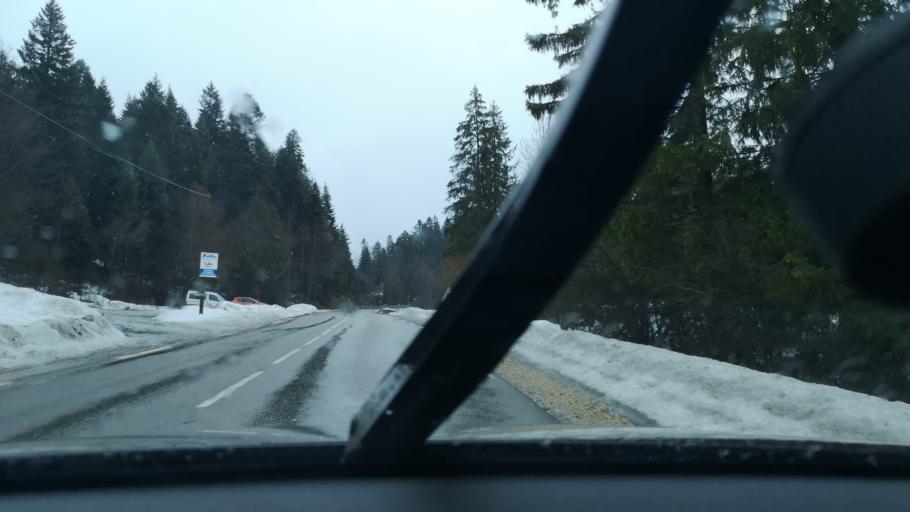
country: FR
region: Franche-Comte
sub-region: Departement du Doubs
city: La Cluse-et-Mijoux
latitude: 46.8610
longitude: 6.3776
